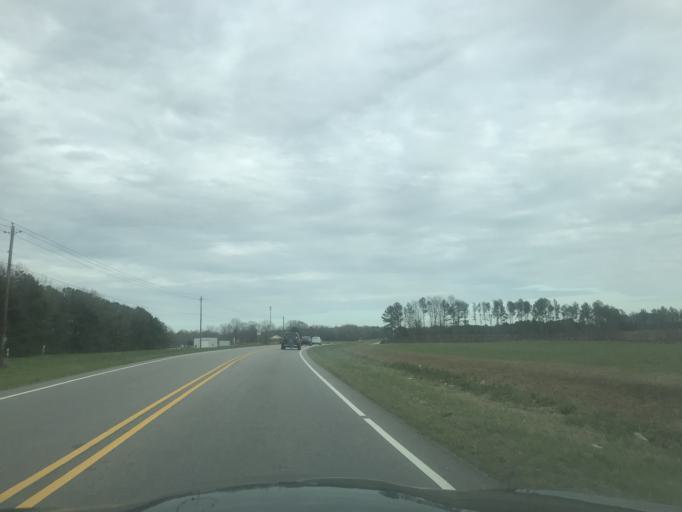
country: US
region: North Carolina
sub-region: Franklin County
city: Franklinton
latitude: 36.0940
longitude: -78.4089
